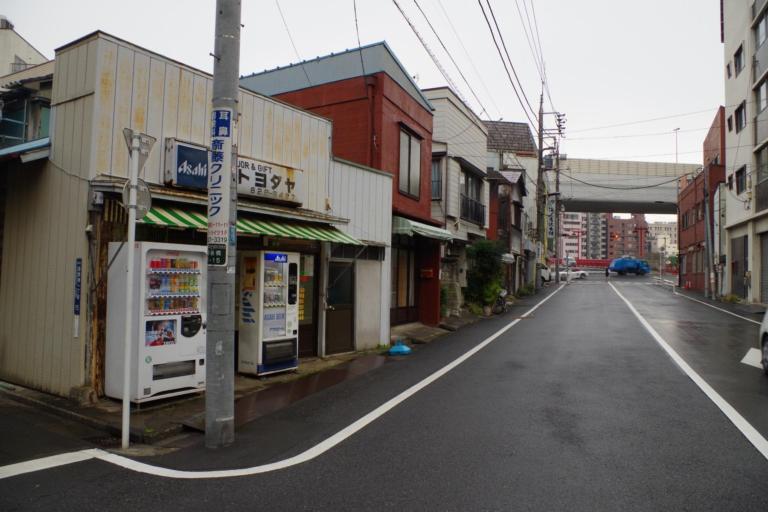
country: JP
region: Tokyo
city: Urayasu
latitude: 35.7090
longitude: 139.8001
